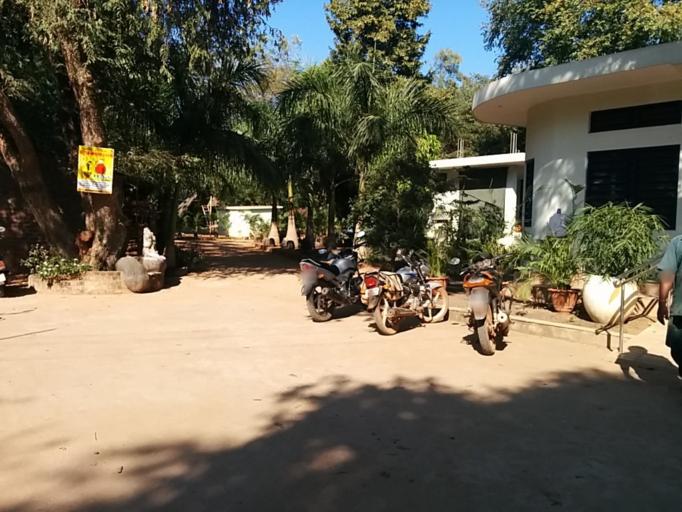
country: IN
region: Tamil Nadu
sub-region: Villupuram
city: Auroville
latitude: 11.9900
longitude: 79.8346
